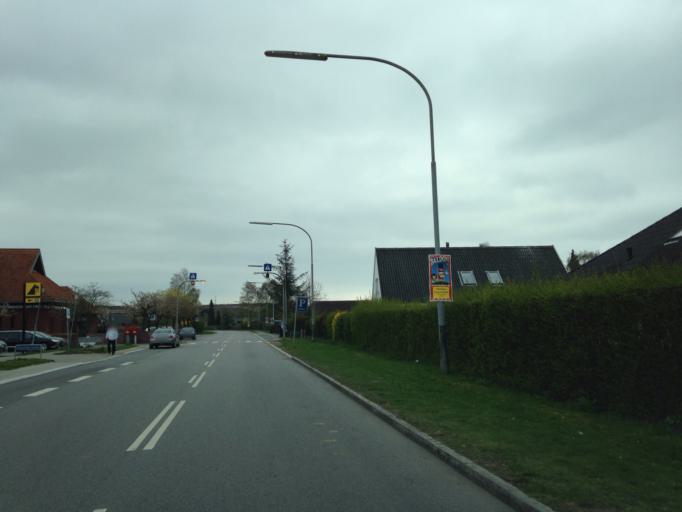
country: DK
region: Zealand
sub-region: Greve Kommune
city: Greve
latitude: 55.5943
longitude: 12.3165
